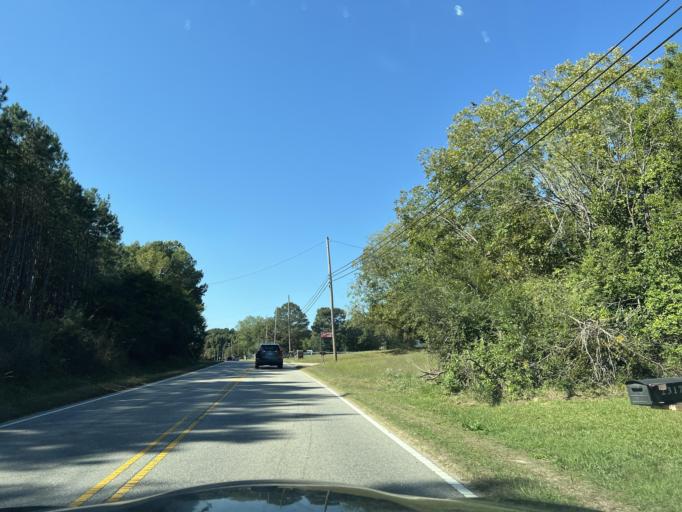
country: US
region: North Carolina
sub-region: Wake County
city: Garner
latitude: 35.6919
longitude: -78.5463
